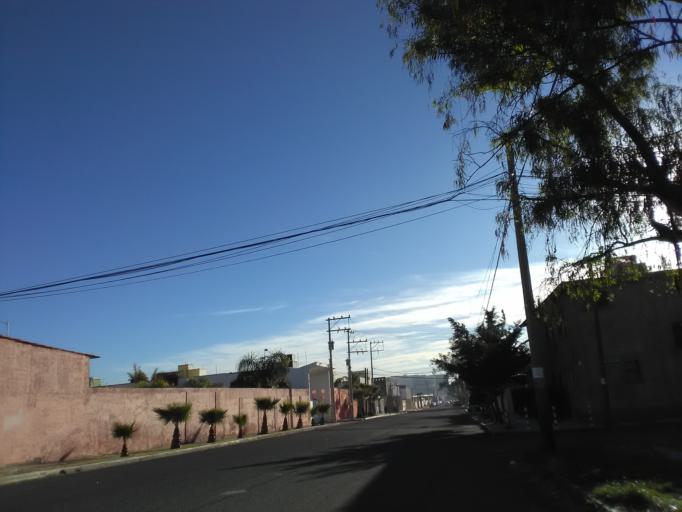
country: MX
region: Durango
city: Victoria de Durango
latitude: 24.0435
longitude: -104.6630
